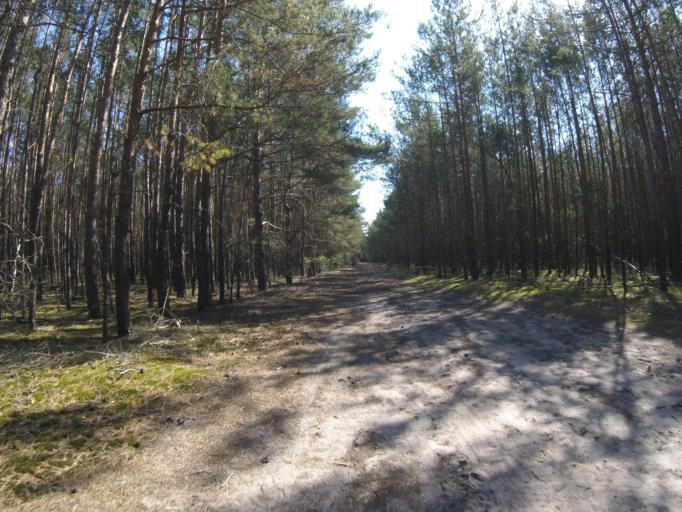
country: DE
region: Brandenburg
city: Bestensee
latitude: 52.2638
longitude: 13.6845
